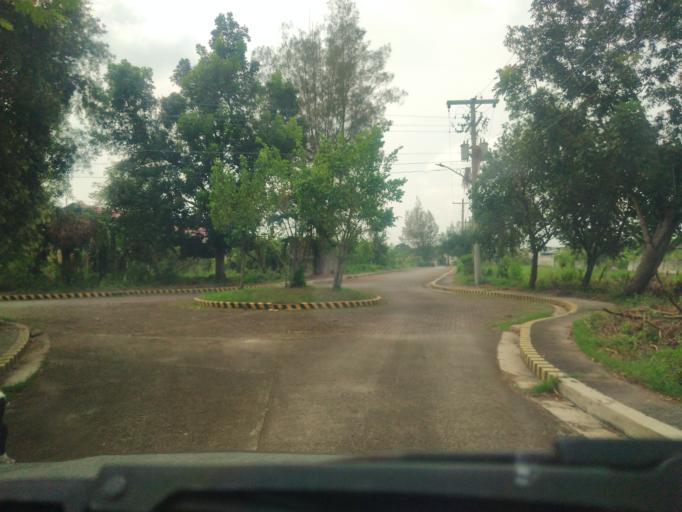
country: PH
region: Central Luzon
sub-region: Province of Pampanga
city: Santo Domingo
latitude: 15.0041
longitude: 120.7244
